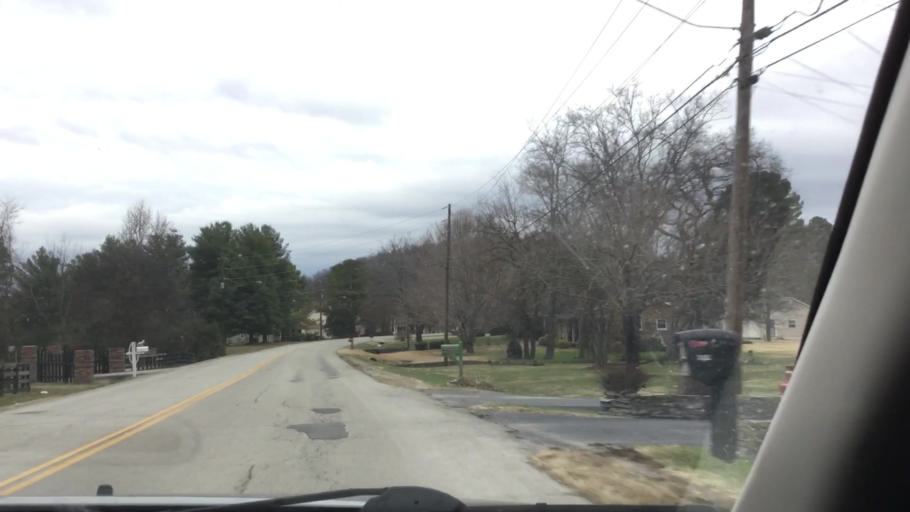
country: US
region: Tennessee
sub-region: Maury County
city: Columbia
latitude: 35.6209
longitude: -87.0959
